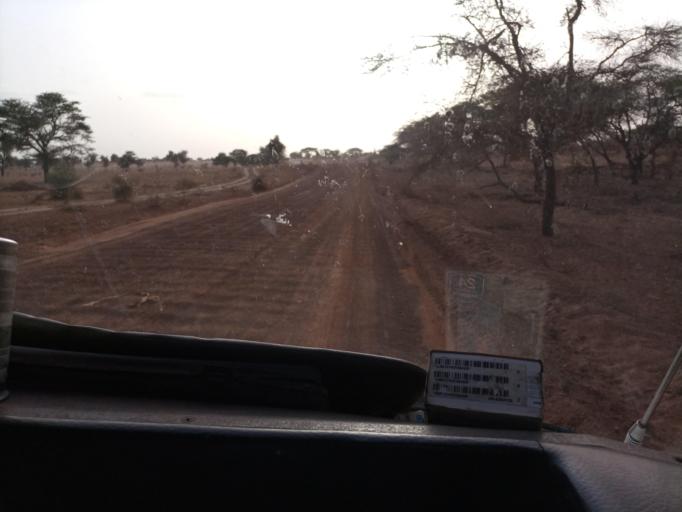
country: SN
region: Louga
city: Dara
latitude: 15.3634
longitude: -15.5524
